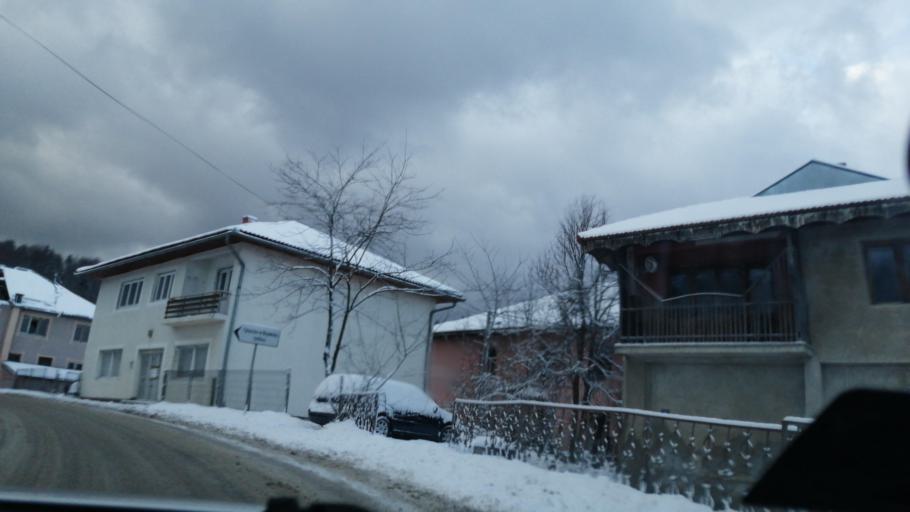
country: BA
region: Republika Srpska
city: Vlasenica
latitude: 44.1781
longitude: 18.9462
